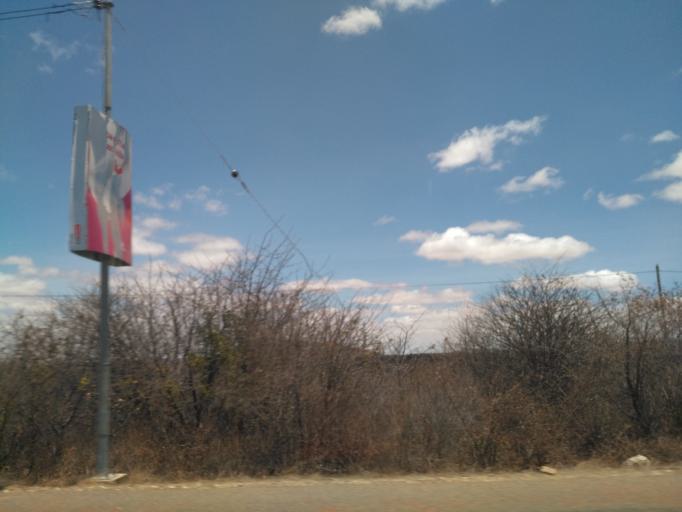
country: TZ
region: Dodoma
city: Kisasa
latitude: -6.2196
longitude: 35.8155
